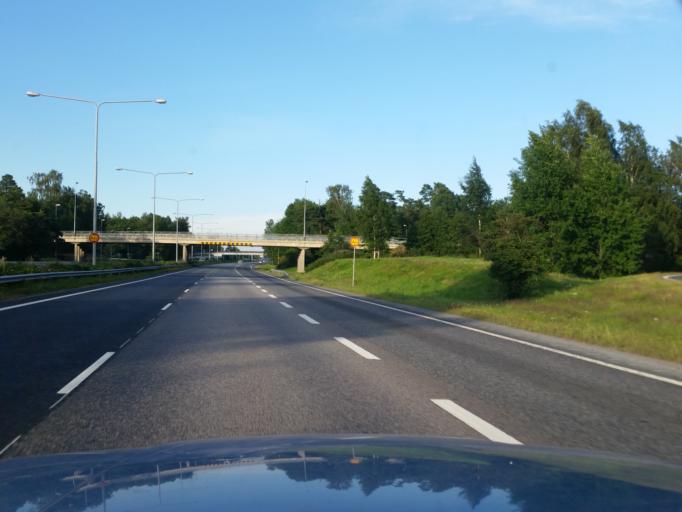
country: FI
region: Uusimaa
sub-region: Helsinki
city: Teekkarikylae
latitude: 60.1634
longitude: 24.8739
